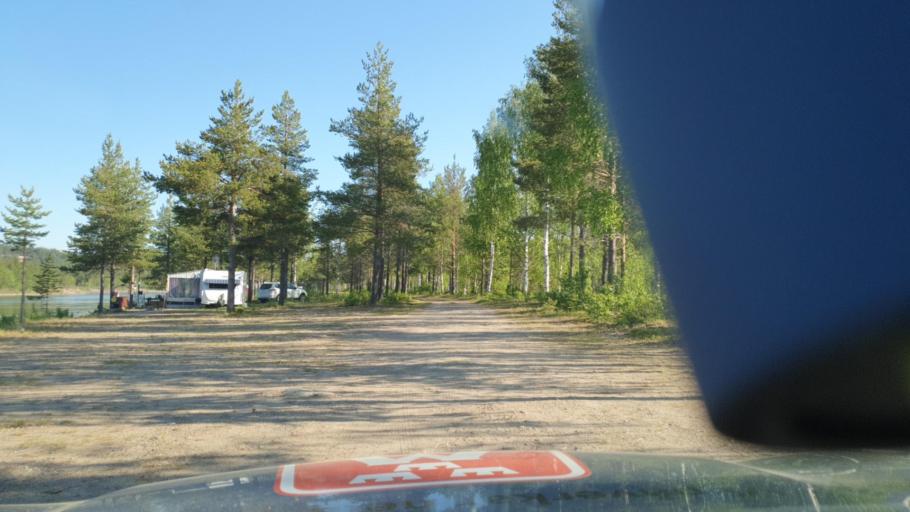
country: SE
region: Norrbotten
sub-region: Alvsbyns Kommun
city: AElvsbyn
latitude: 66.2159
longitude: 20.8610
